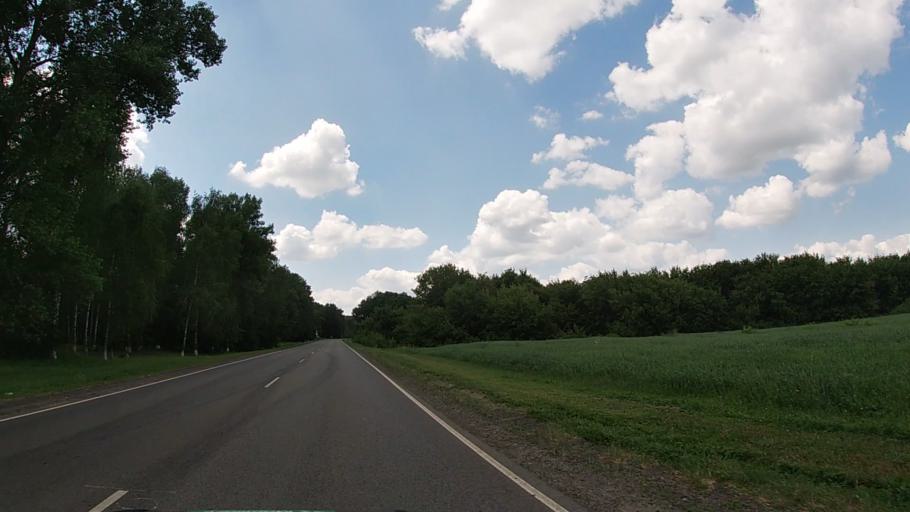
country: RU
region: Belgorod
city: Grayvoron
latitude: 50.4967
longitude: 35.7147
